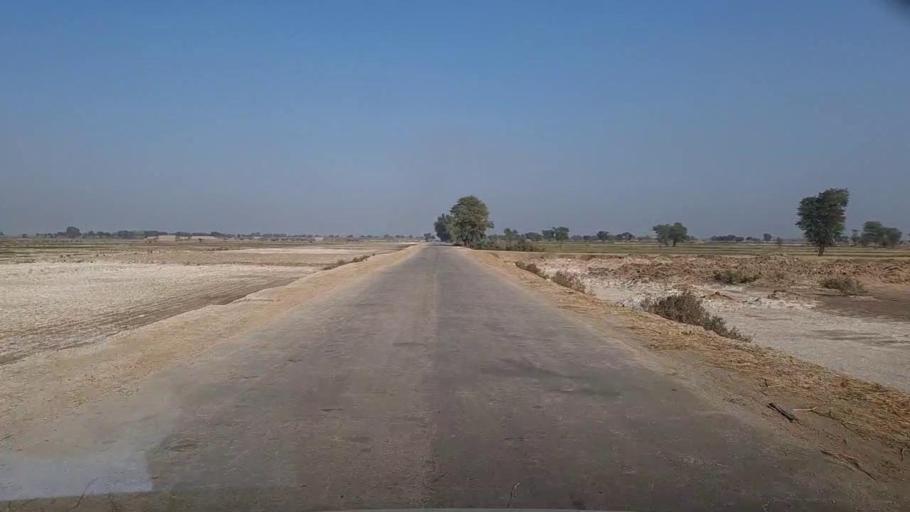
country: PK
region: Sindh
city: Dadu
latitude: 26.8420
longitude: 67.7846
